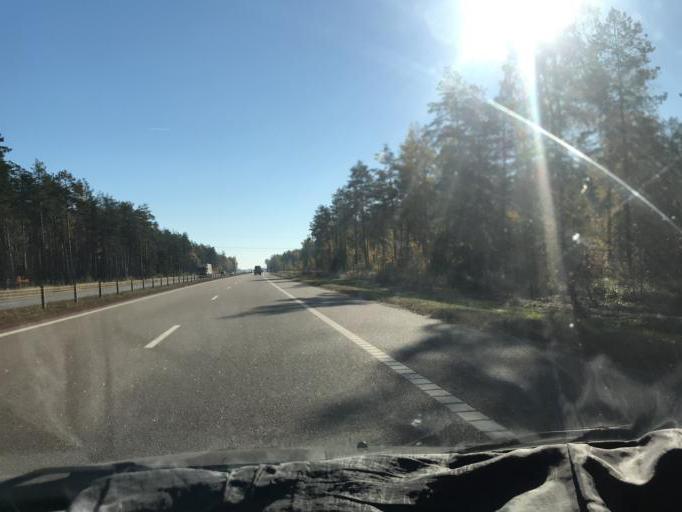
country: BY
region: Mogilev
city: Yalizava
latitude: 53.2611
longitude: 28.8968
